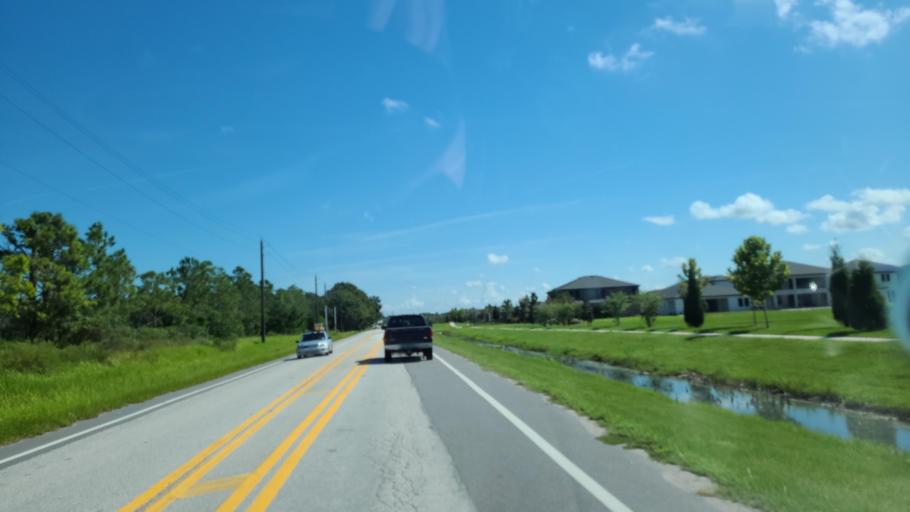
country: US
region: Florida
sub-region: Hillsborough County
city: Boyette
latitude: 27.8093
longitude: -82.2358
